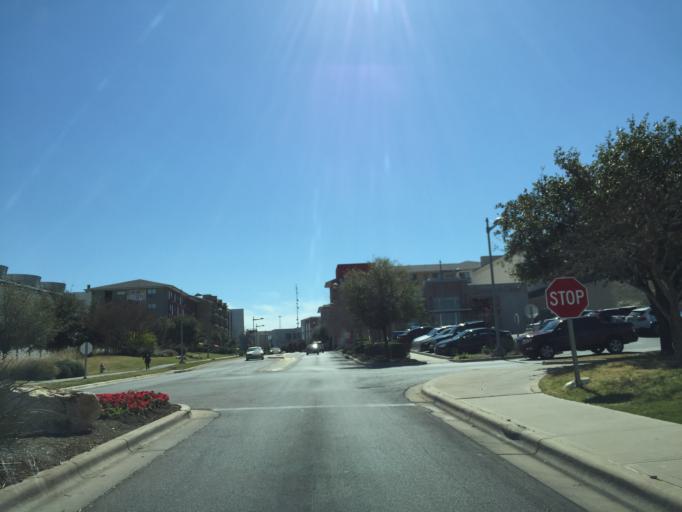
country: US
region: Texas
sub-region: Williamson County
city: Jollyville
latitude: 30.3984
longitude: -97.7259
